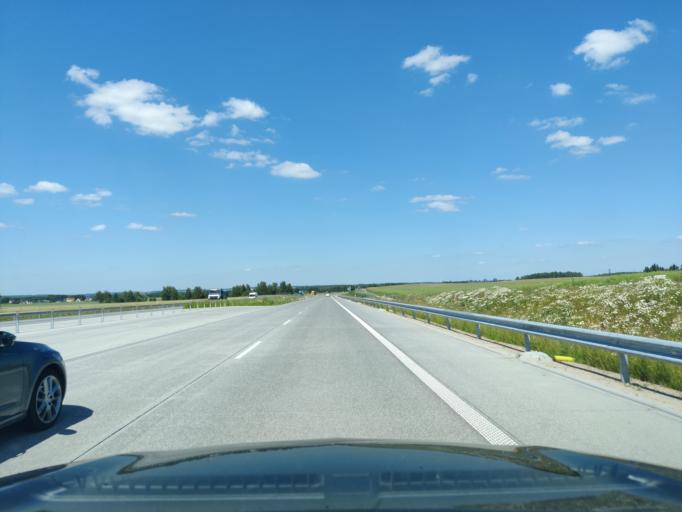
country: PL
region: Masovian Voivodeship
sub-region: Powiat mlawski
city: Wisniewo
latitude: 53.0615
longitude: 20.3661
